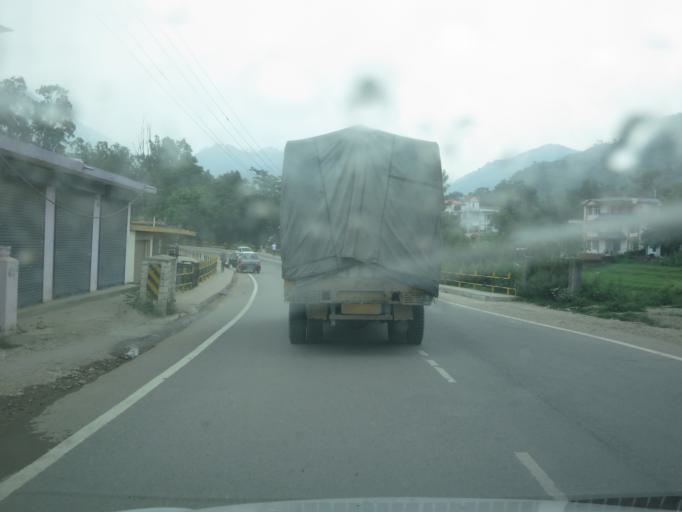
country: IN
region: Himachal Pradesh
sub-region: Mandi
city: Sundarnagar
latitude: 31.5179
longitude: 76.8821
